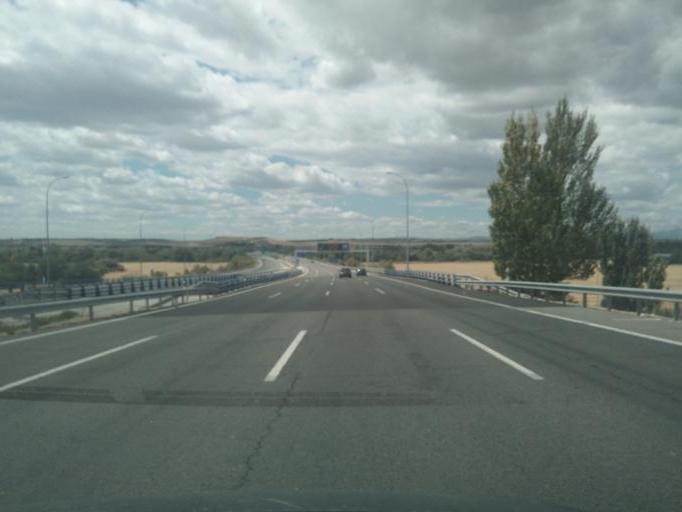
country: ES
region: Madrid
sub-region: Provincia de Madrid
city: Paracuellos de Jarama
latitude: 40.5441
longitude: -3.5485
